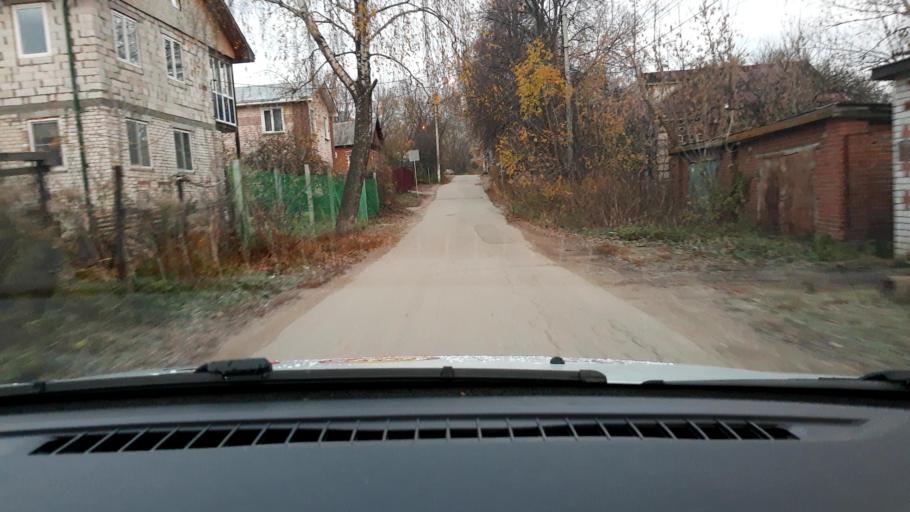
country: RU
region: Nizjnij Novgorod
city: Afonino
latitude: 56.2707
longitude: 44.0921
